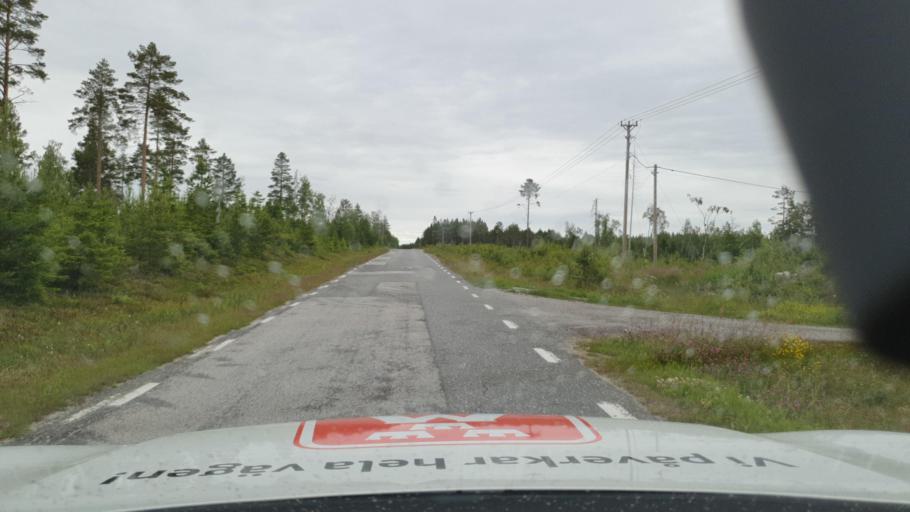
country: SE
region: Vaesterbotten
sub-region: Nordmalings Kommun
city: Nordmaling
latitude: 63.4505
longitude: 19.4679
